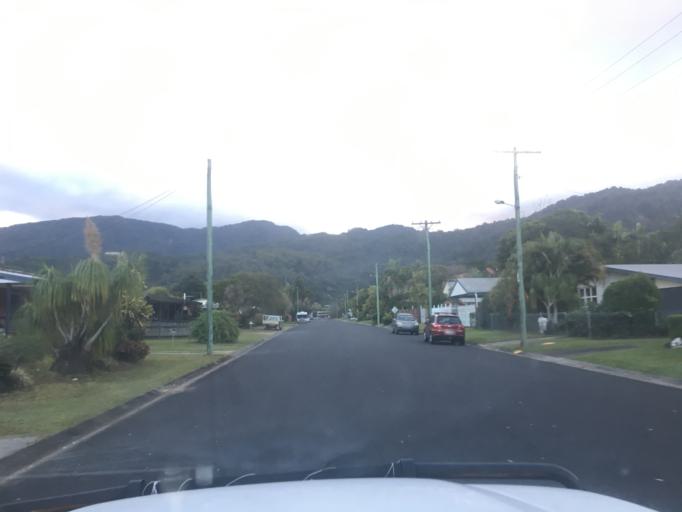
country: AU
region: Queensland
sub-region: Cairns
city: Woree
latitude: -16.9427
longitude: 145.7337
